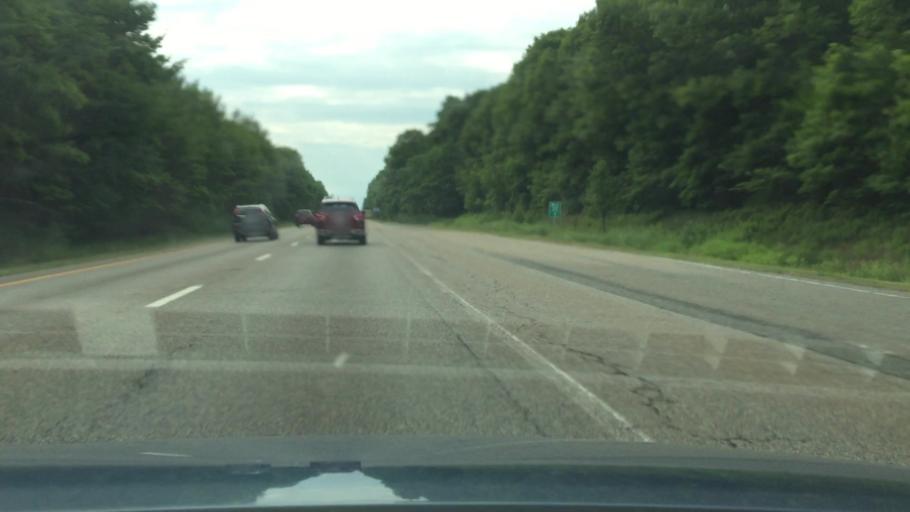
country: US
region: Massachusetts
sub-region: Plymouth County
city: Hanover
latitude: 42.1307
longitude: -70.8069
